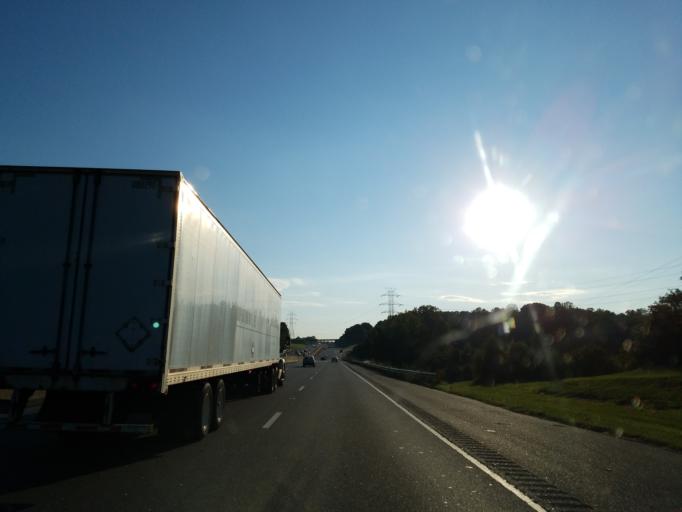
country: US
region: North Carolina
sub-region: Gaston County
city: Bessemer City
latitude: 35.2692
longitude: -81.2499
